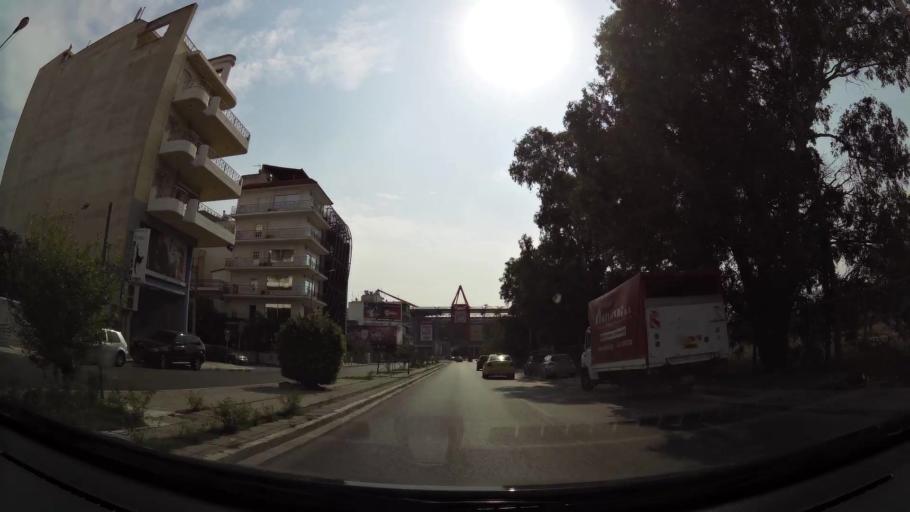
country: GR
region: Attica
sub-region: Nomarchia Athinas
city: Moskhaton
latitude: 37.9493
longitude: 23.6638
